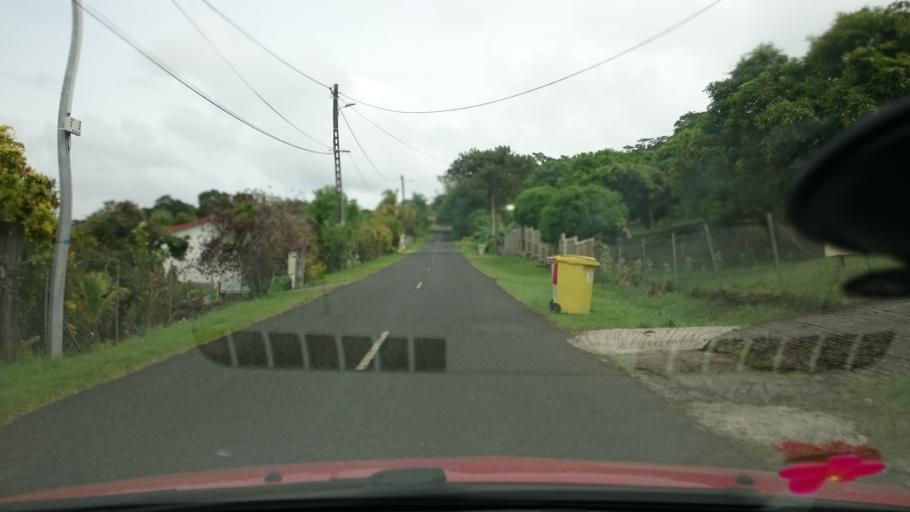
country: MQ
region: Martinique
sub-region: Martinique
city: Sainte-Luce
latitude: 14.4956
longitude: -60.9256
